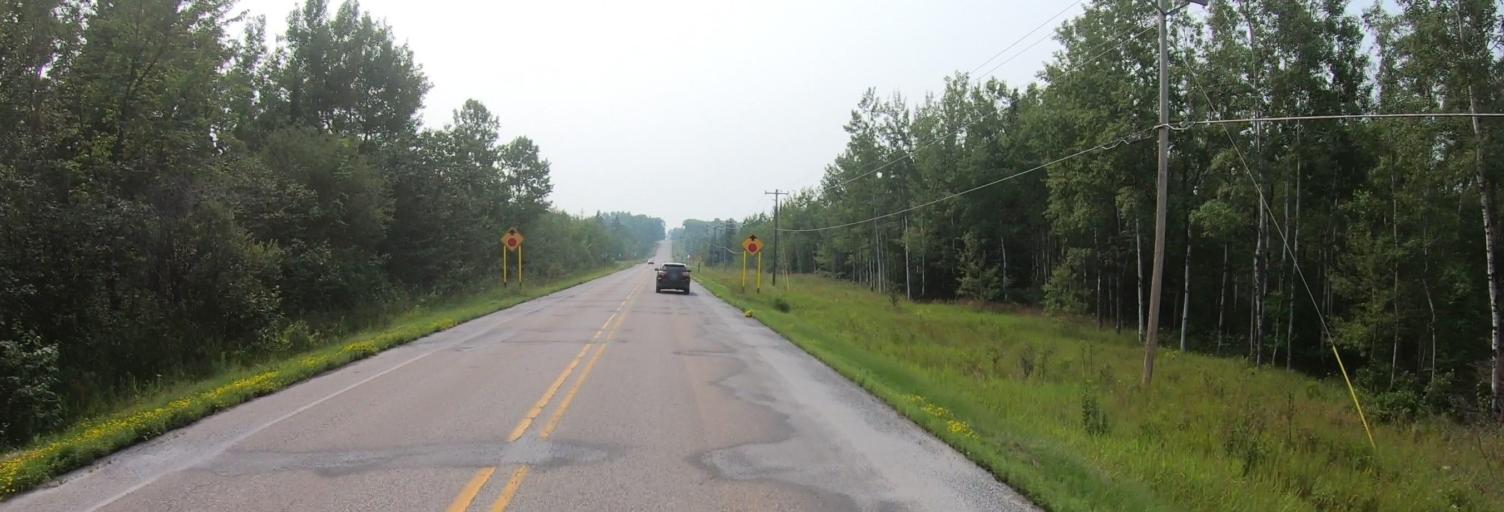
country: US
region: Michigan
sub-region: Chippewa County
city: Sault Ste. Marie
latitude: 46.4629
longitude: -84.3194
